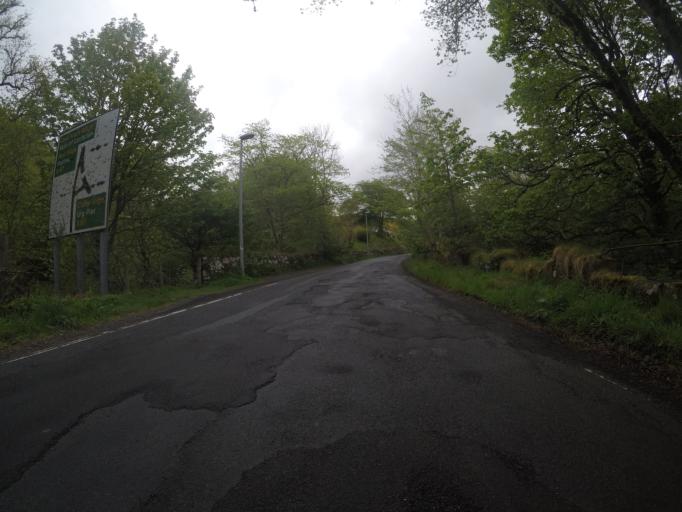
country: GB
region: Scotland
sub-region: Highland
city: Portree
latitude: 57.5923
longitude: -6.3617
